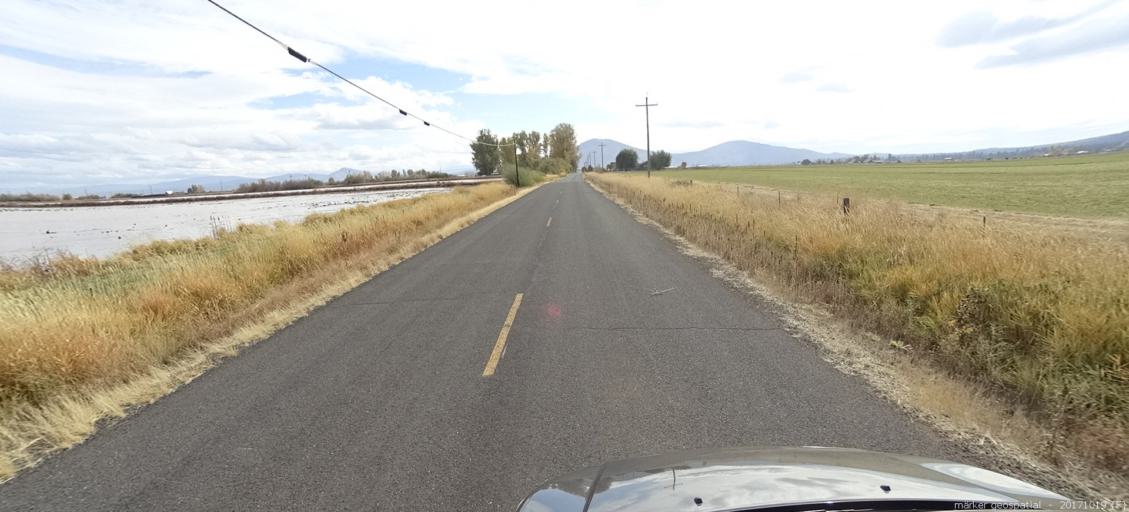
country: US
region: California
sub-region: Shasta County
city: Burney
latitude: 41.1015
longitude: -121.4932
